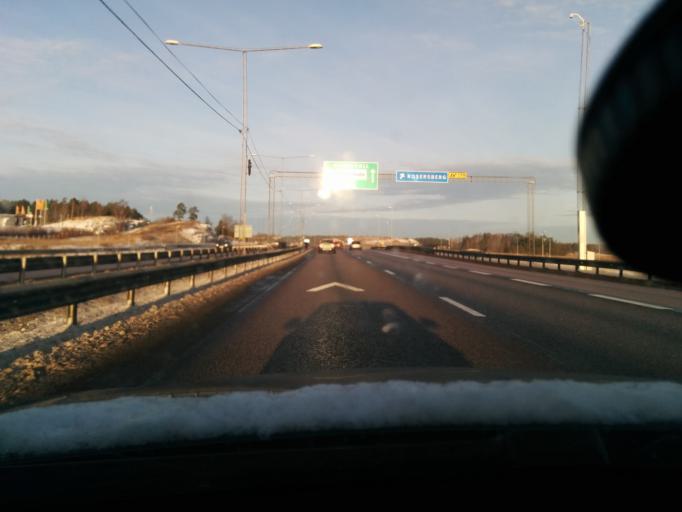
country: SE
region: Stockholm
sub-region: Sigtuna Kommun
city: Rosersberg
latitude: 59.5733
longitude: 17.8995
